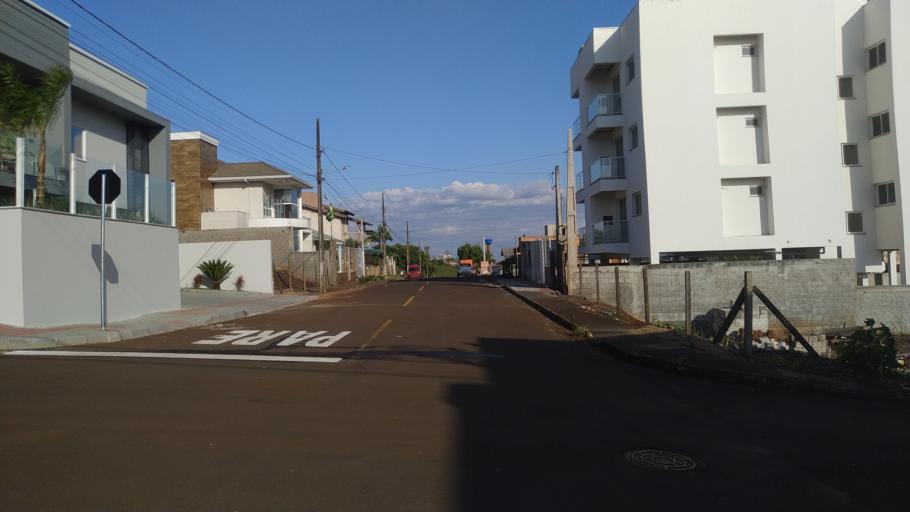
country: BR
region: Santa Catarina
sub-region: Chapeco
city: Chapeco
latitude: -27.0687
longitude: -52.6092
